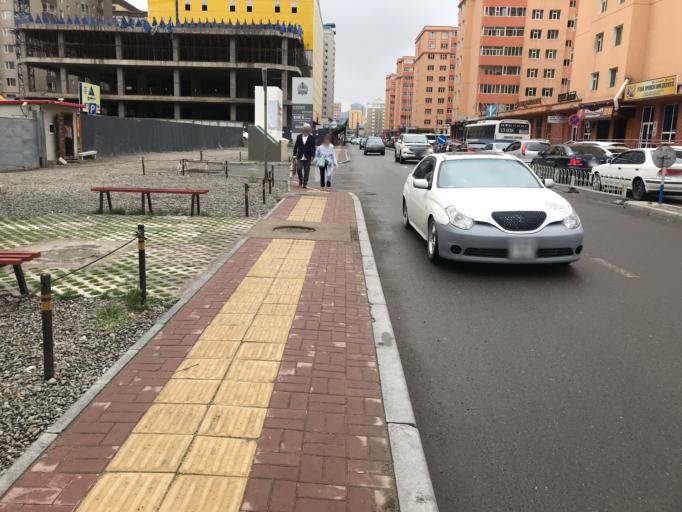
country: MN
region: Ulaanbaatar
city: Ulaanbaatar
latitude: 47.9047
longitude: 106.9362
